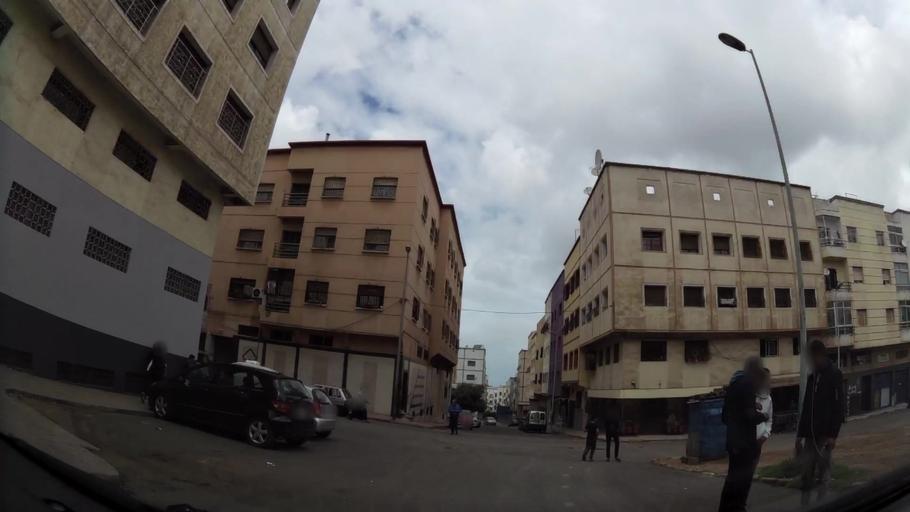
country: MA
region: Grand Casablanca
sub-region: Casablanca
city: Casablanca
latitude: 33.5347
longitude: -7.5866
